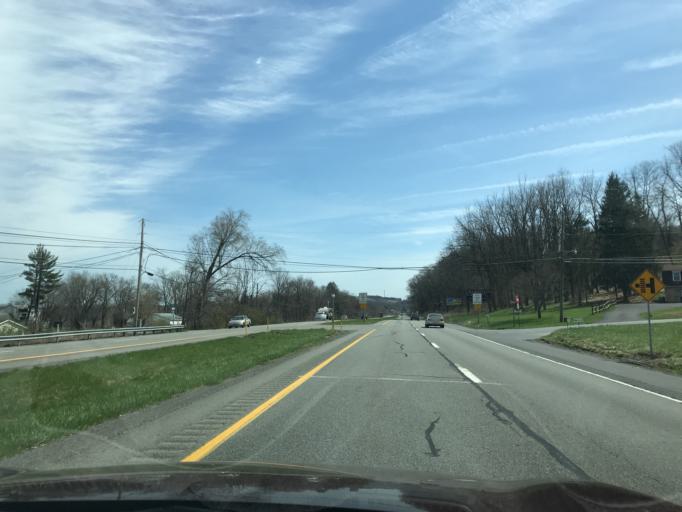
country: US
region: Pennsylvania
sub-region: Union County
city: Lewisburg
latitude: 40.9203
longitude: -76.8589
